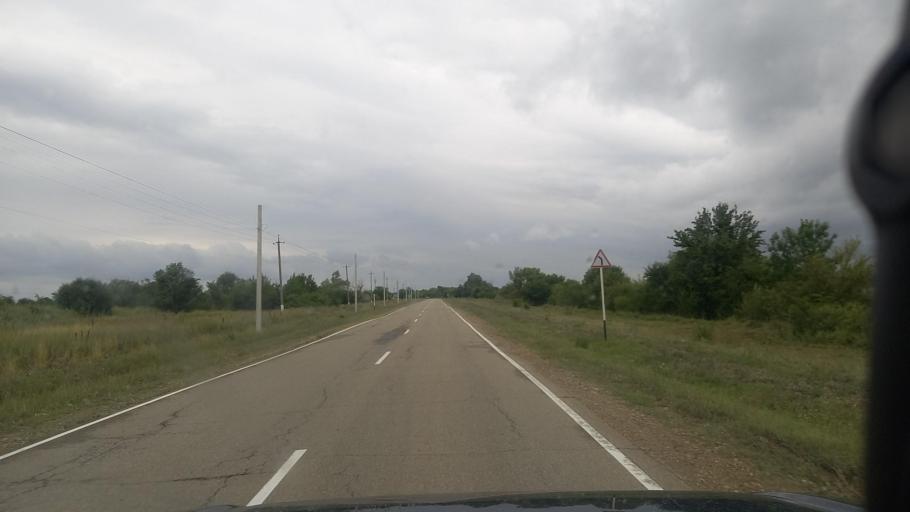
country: RU
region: Adygeya
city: Adygeysk
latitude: 44.8847
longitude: 39.2473
